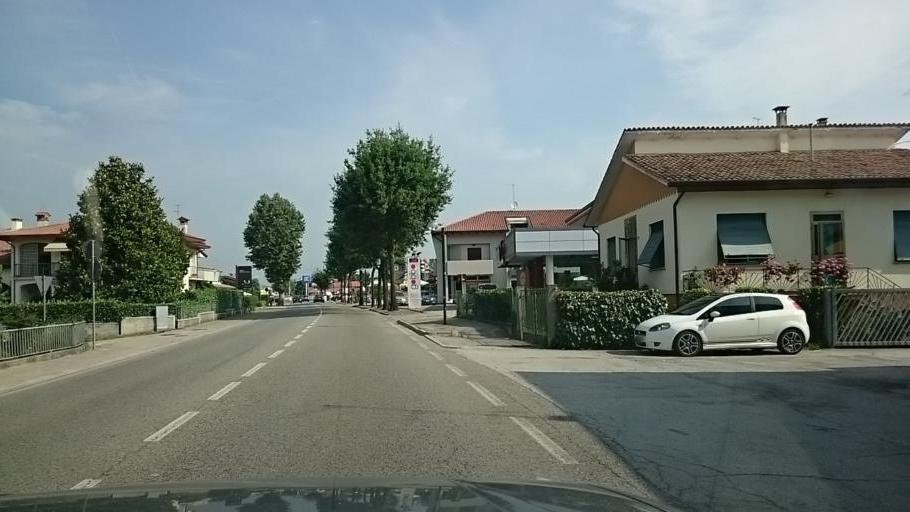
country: IT
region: Veneto
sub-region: Provincia di Treviso
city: Resana
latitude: 45.6365
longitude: 11.9548
